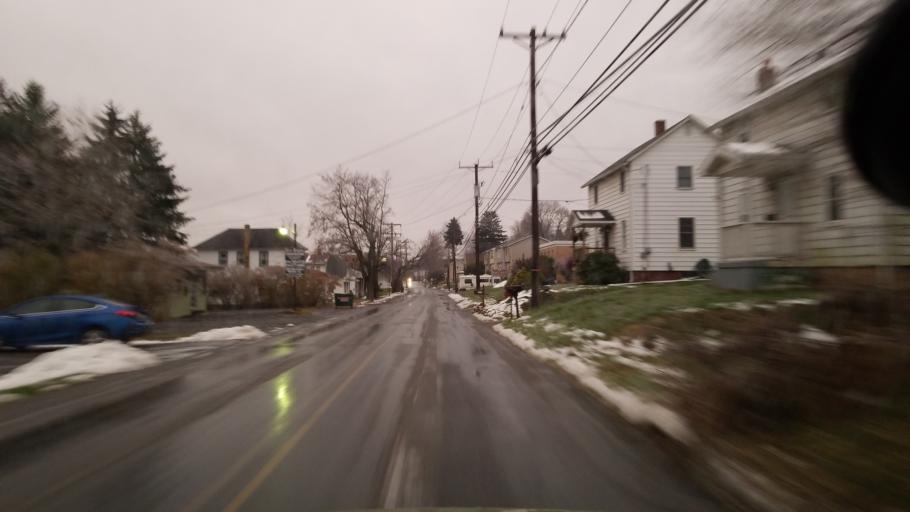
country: US
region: Pennsylvania
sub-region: Clearfield County
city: Clearfield
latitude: 41.0365
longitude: -78.4527
